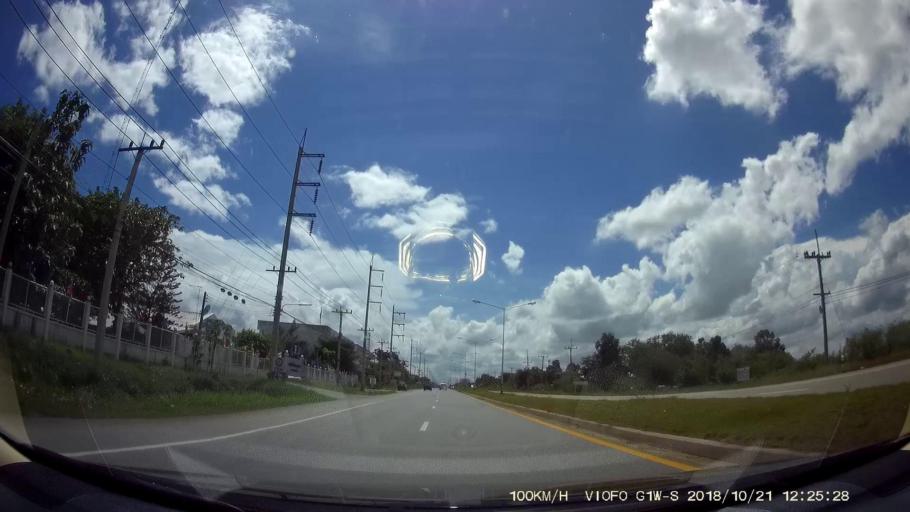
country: TH
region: Nakhon Ratchasima
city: Dan Khun Thot
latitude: 15.2209
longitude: 101.7717
